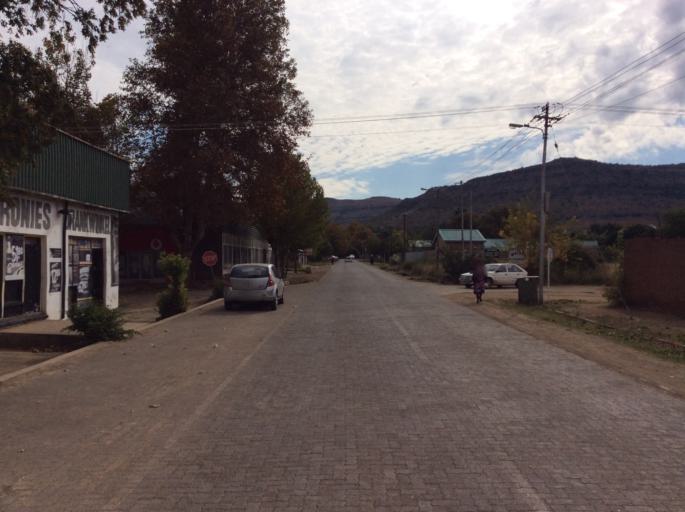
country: LS
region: Mafeteng
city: Mafeteng
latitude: -29.7297
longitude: 27.0366
